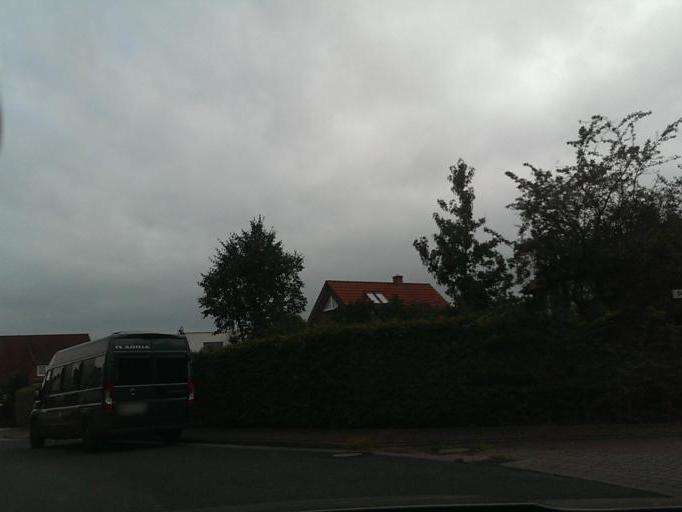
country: DE
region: Lower Saxony
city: Elze
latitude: 52.5260
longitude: 9.7371
